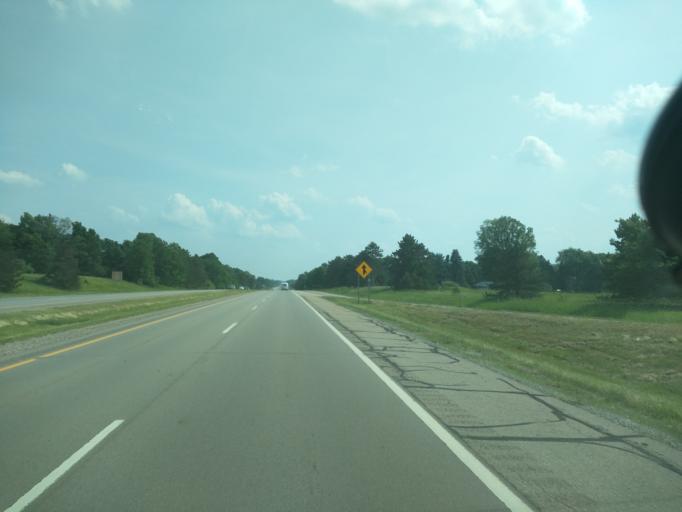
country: US
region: Michigan
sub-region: Ingham County
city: Leslie
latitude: 42.3762
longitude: -84.4292
